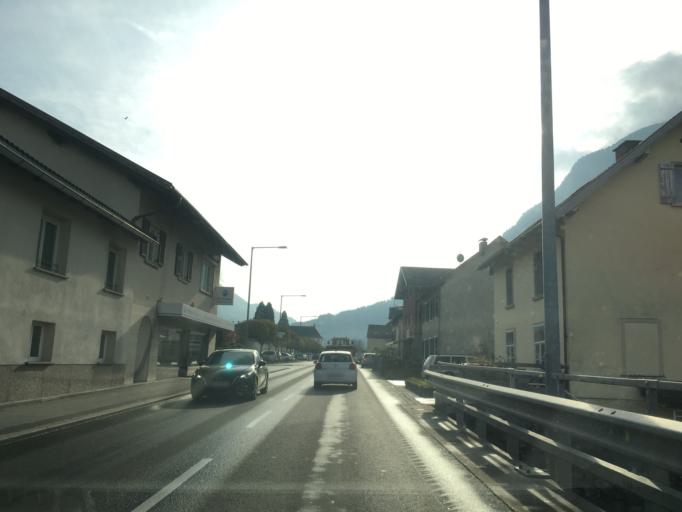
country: AT
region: Vorarlberg
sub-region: Politischer Bezirk Bludenz
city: Bludenz
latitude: 47.1488
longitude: 9.8269
